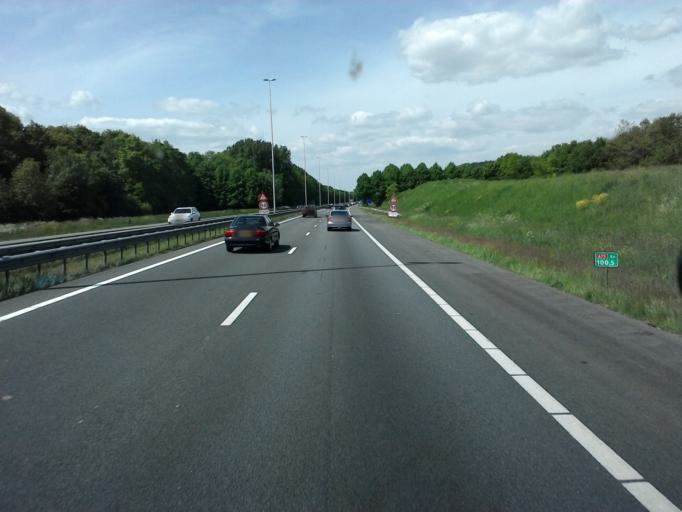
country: NL
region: Gelderland
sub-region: Gemeente Nijmegen
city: Lindenholt
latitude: 51.8105
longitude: 5.7824
